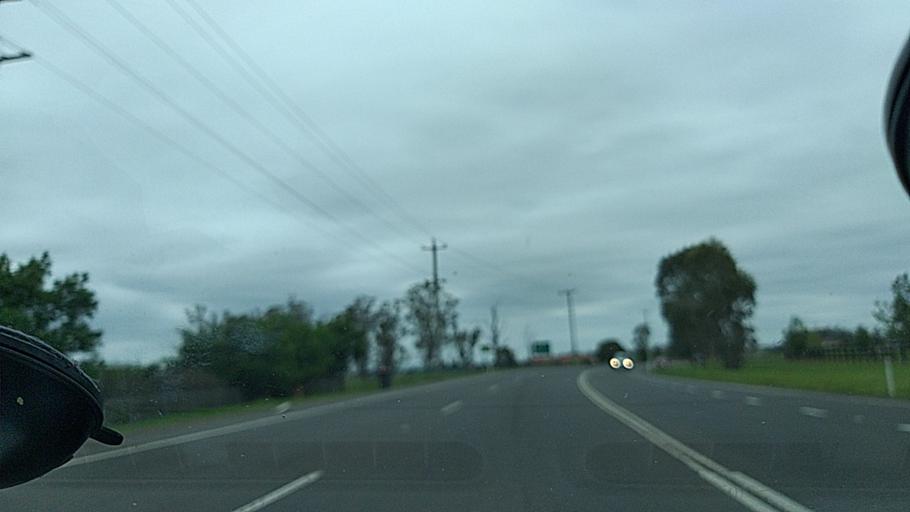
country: AU
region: New South Wales
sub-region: Liverpool
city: Luddenham
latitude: -33.8652
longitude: 150.6978
